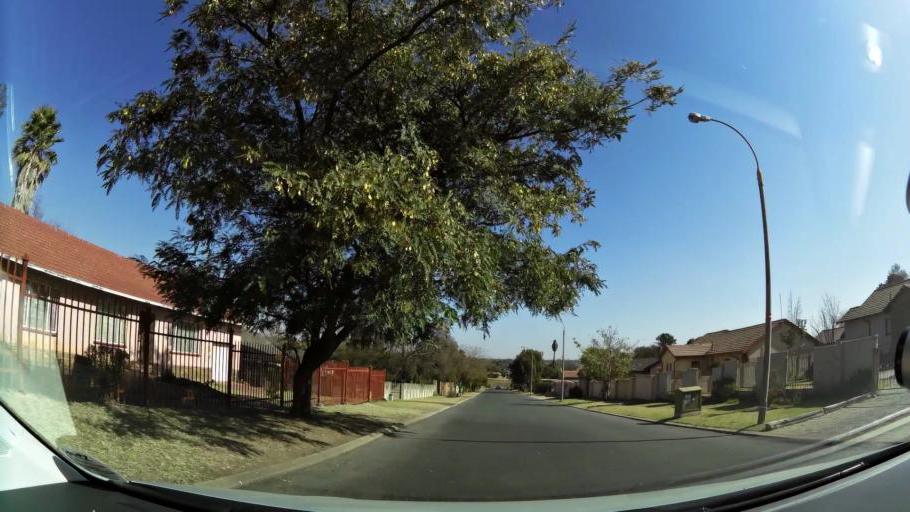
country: ZA
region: Gauteng
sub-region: Ekurhuleni Metropolitan Municipality
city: Tembisa
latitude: -26.0388
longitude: 28.2352
